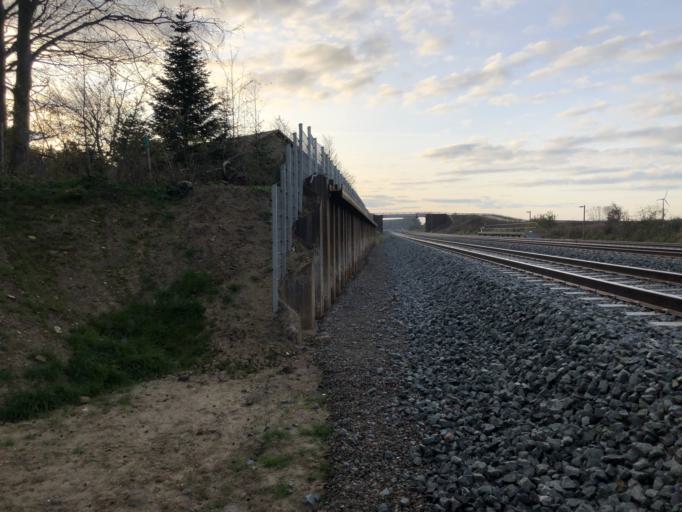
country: DK
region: Zealand
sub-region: Guldborgsund Kommune
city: Norre Alslev
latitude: 54.9354
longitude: 11.8699
